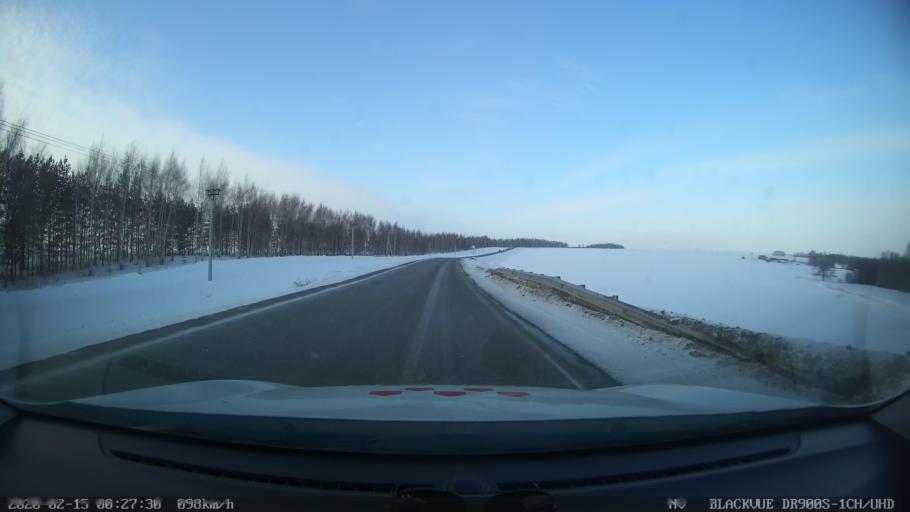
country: RU
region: Tatarstan
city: Verkhniy Uslon
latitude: 55.6291
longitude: 48.8737
